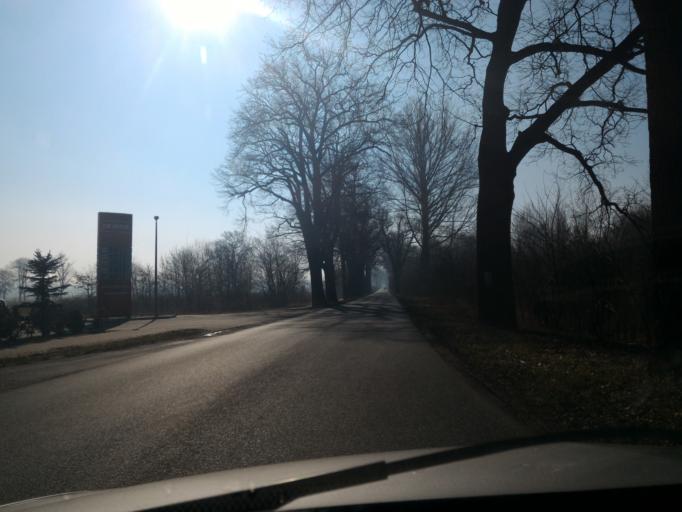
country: DE
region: Saxony
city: Zittau
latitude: 50.8833
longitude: 14.8195
